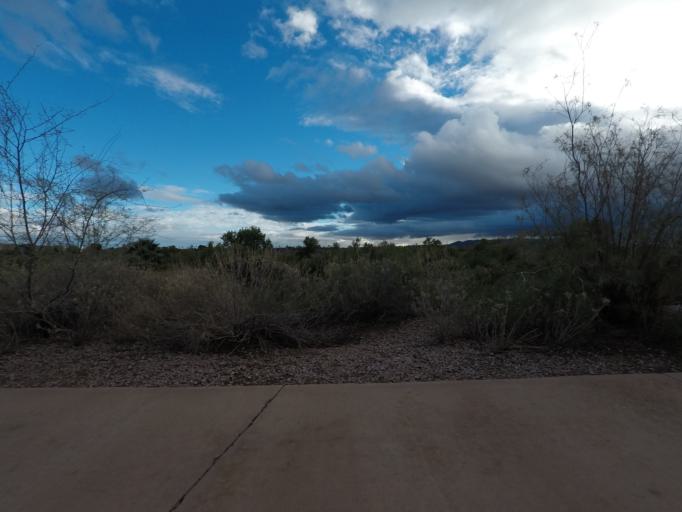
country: US
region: Arizona
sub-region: Maricopa County
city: Tempe Junction
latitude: 33.4358
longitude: -111.9544
